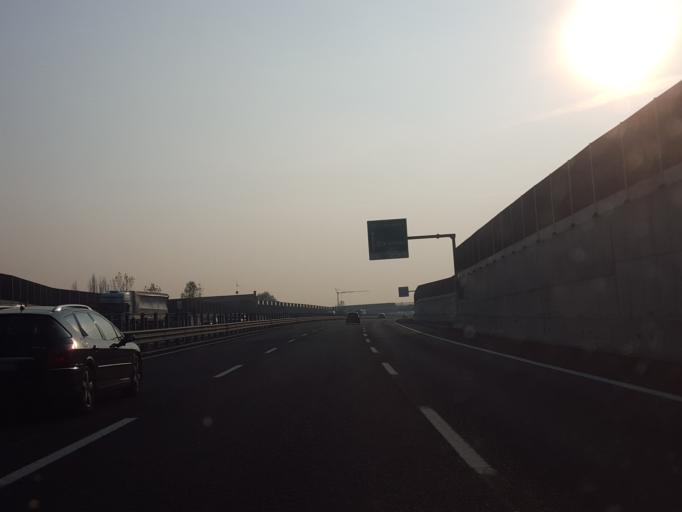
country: IT
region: Veneto
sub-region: Provincia di Venezia
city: Spinea-Orgnano
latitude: 45.4921
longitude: 12.1383
